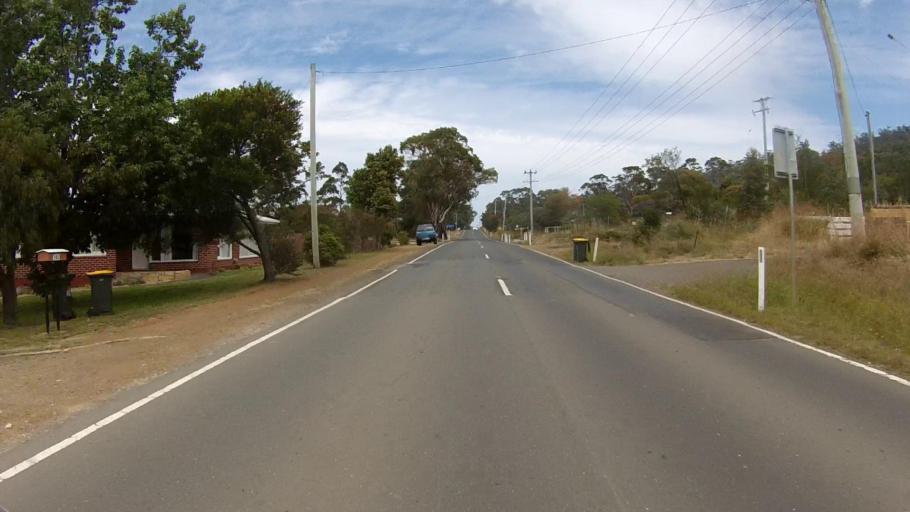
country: AU
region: Tasmania
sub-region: Clarence
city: Acton Park
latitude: -42.8944
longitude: 147.4815
